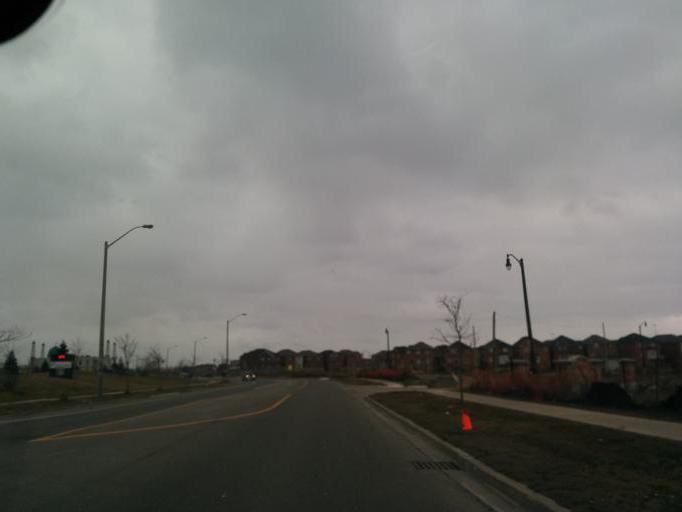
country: CA
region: Ontario
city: Brampton
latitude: 43.7394
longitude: -79.7722
